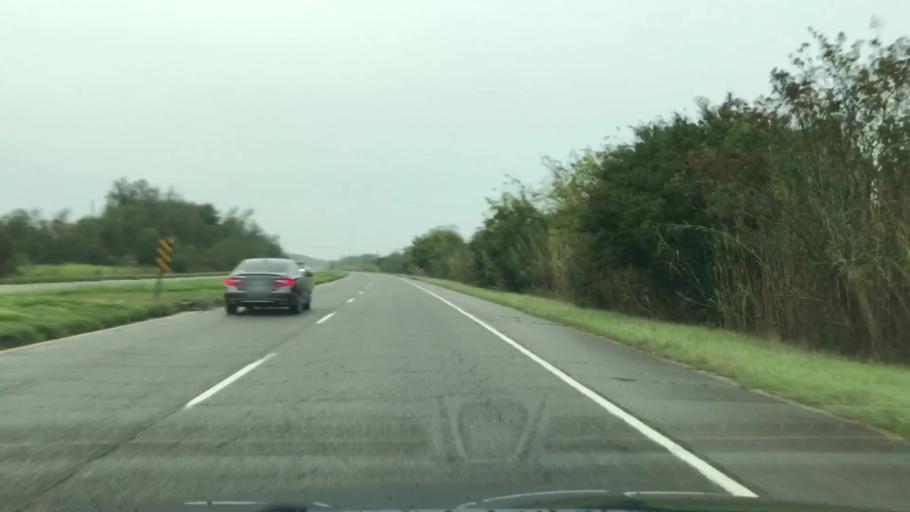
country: US
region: Louisiana
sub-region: Saint Charles Parish
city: Des Allemands
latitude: 29.7967
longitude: -90.5073
